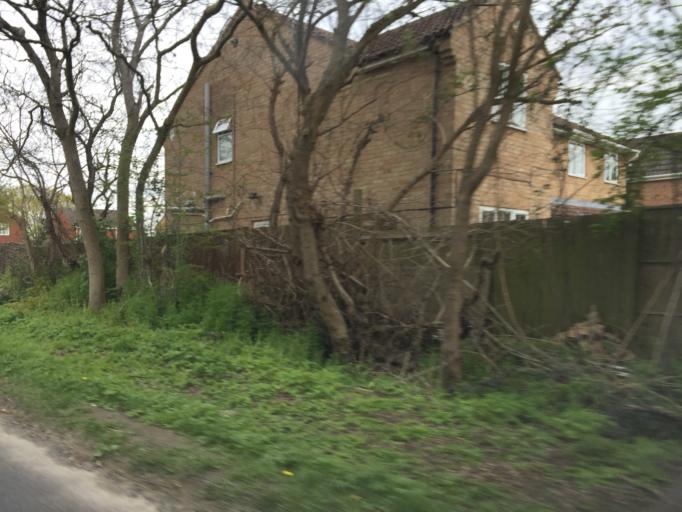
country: GB
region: England
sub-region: Oxfordshire
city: Bicester
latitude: 51.9074
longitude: -1.1745
